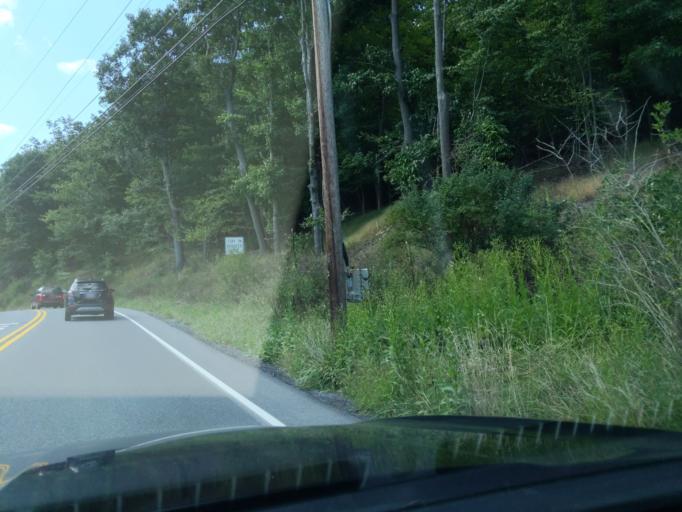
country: US
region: Pennsylvania
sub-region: Blair County
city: Greenwood
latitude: 40.5081
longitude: -78.3486
